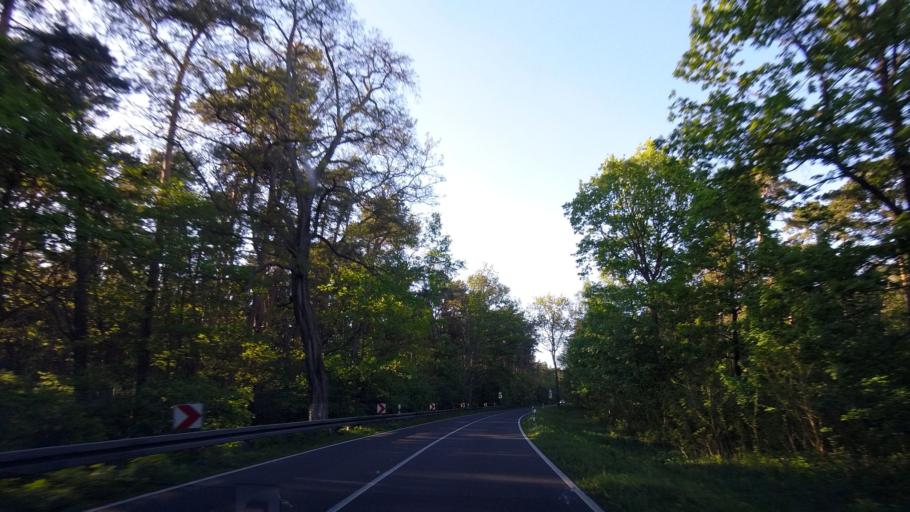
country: DE
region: Brandenburg
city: Golssen
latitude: 51.9887
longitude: 13.5603
